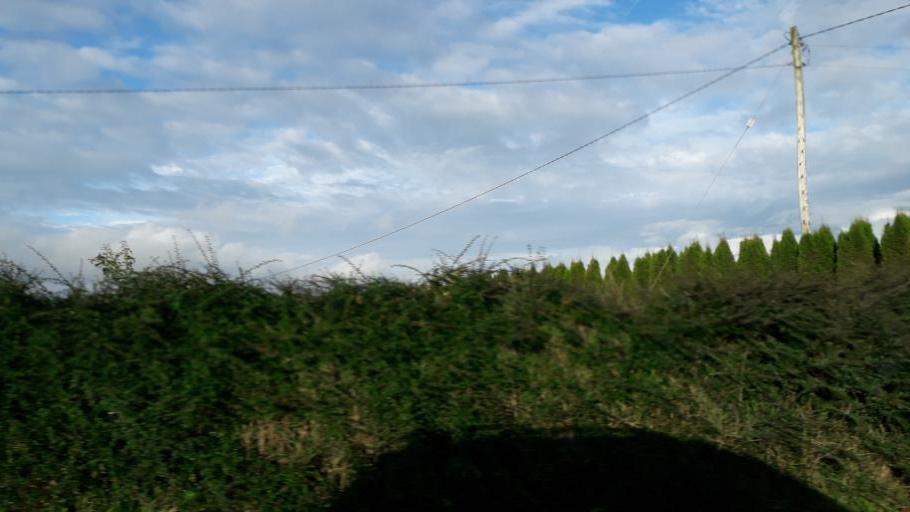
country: IE
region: Connaught
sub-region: Roscommon
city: Roscommon
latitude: 53.7887
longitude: -8.2706
